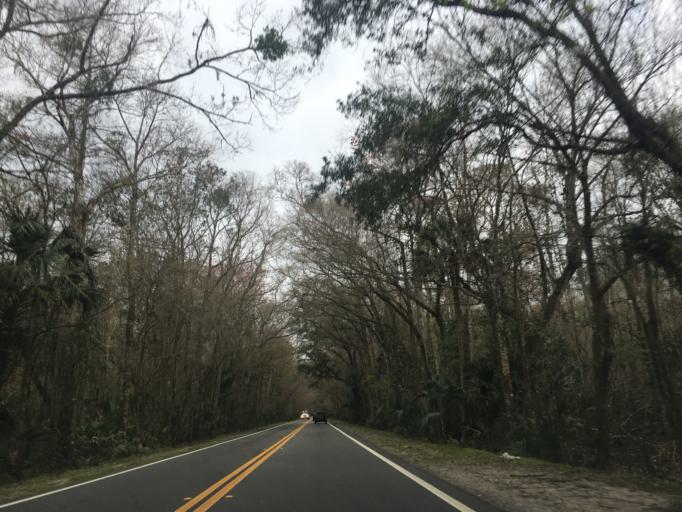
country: US
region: Florida
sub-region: Saint Johns County
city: Villano Beach
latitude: 30.0011
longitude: -81.4170
